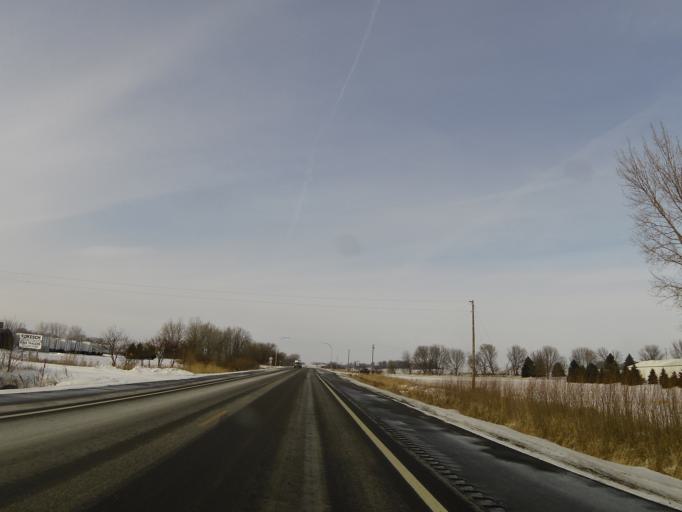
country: US
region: Minnesota
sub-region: McLeod County
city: Hutchinson
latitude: 44.8972
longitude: -94.4312
